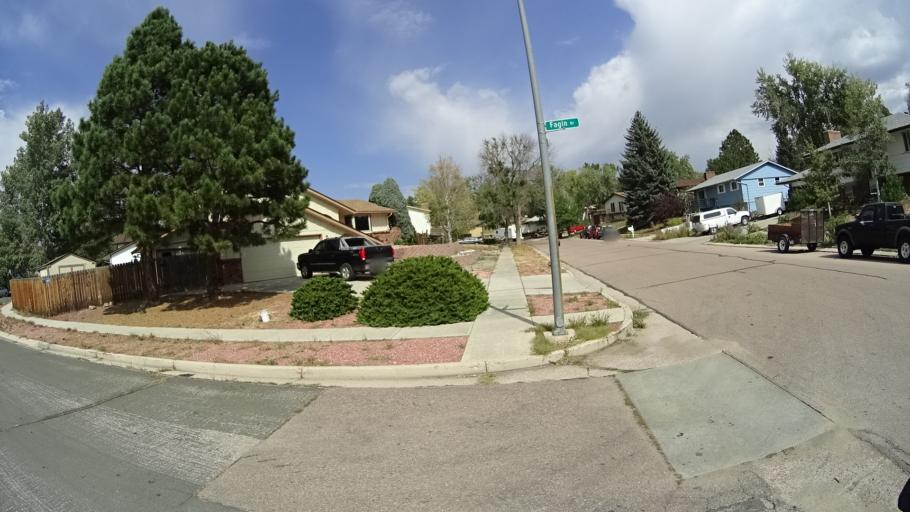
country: US
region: Colorado
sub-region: El Paso County
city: Cimarron Hills
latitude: 38.8501
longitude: -104.7422
